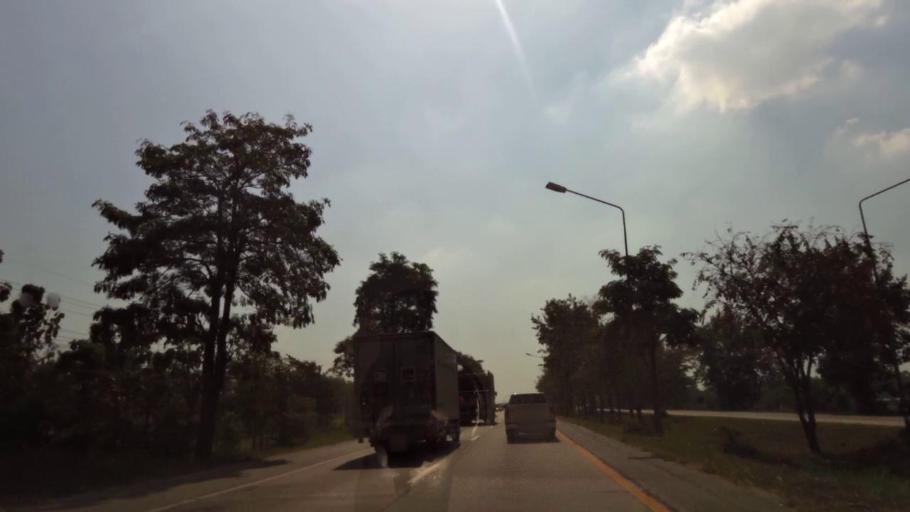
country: TH
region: Phichit
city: Wachira Barami
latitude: 16.5313
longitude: 100.1436
